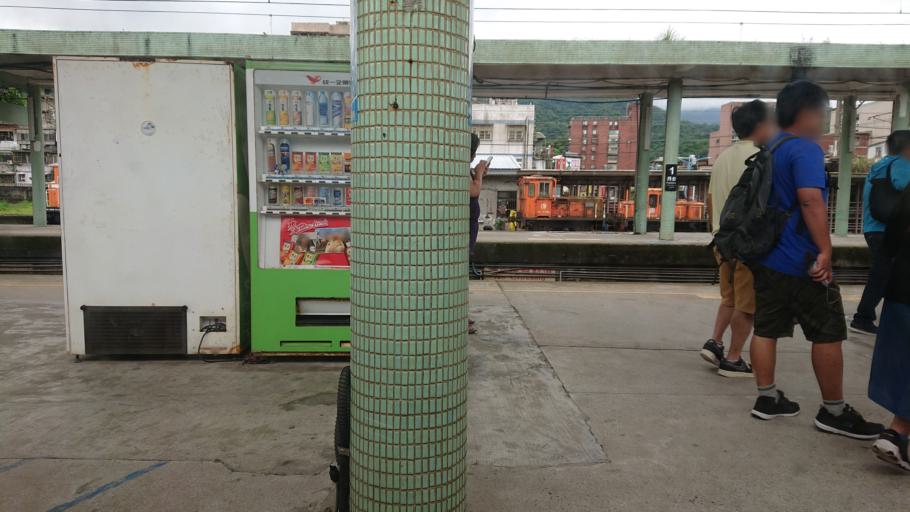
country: TW
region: Taiwan
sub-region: Keelung
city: Keelung
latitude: 25.1090
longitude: 121.8065
